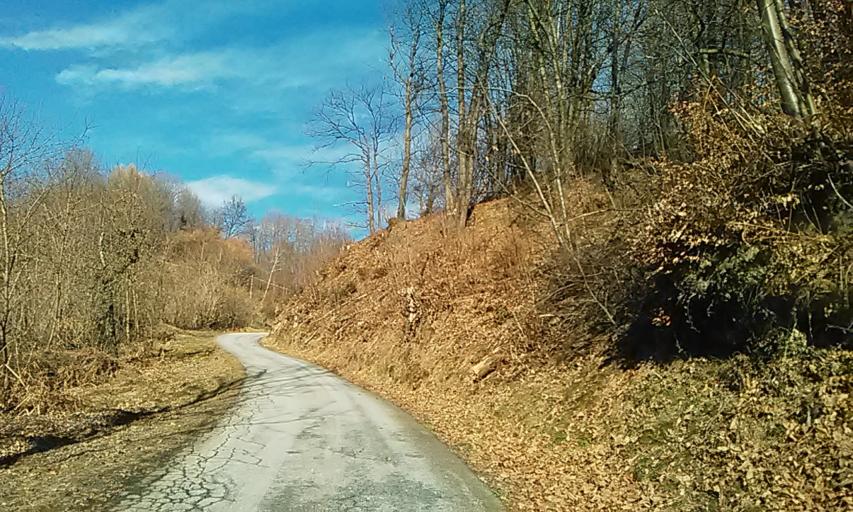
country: IT
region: Piedmont
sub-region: Provincia di Vercelli
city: Valduggia
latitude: 45.7322
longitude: 8.3172
